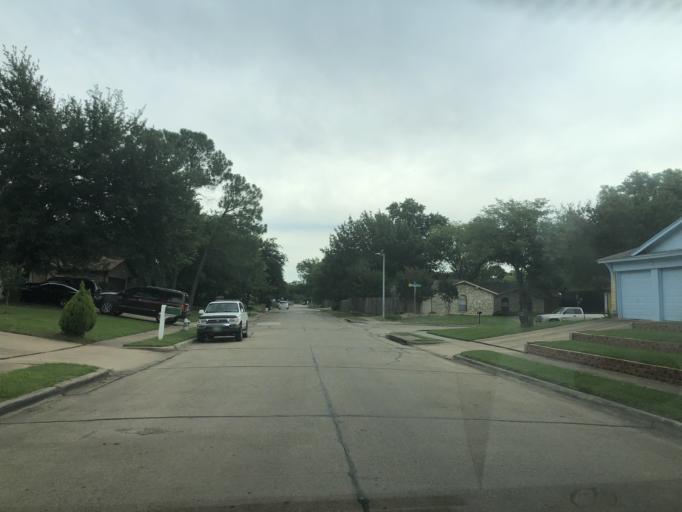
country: US
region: Texas
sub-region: Dallas County
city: Irving
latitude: 32.7853
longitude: -96.9676
